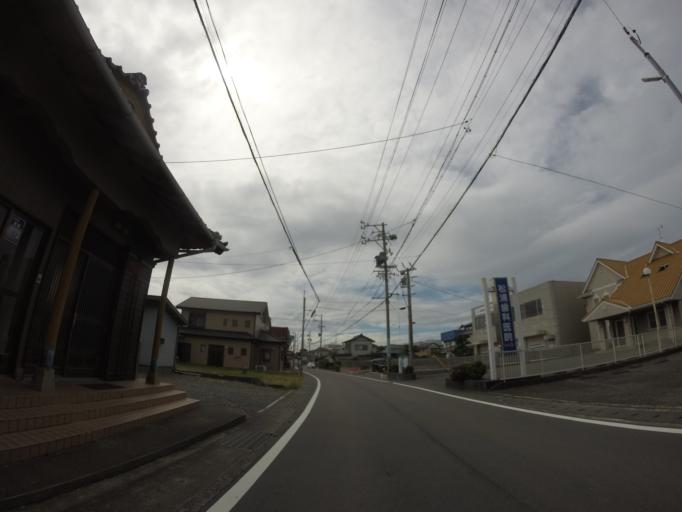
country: JP
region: Shizuoka
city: Oyama
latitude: 34.6095
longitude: 138.2082
